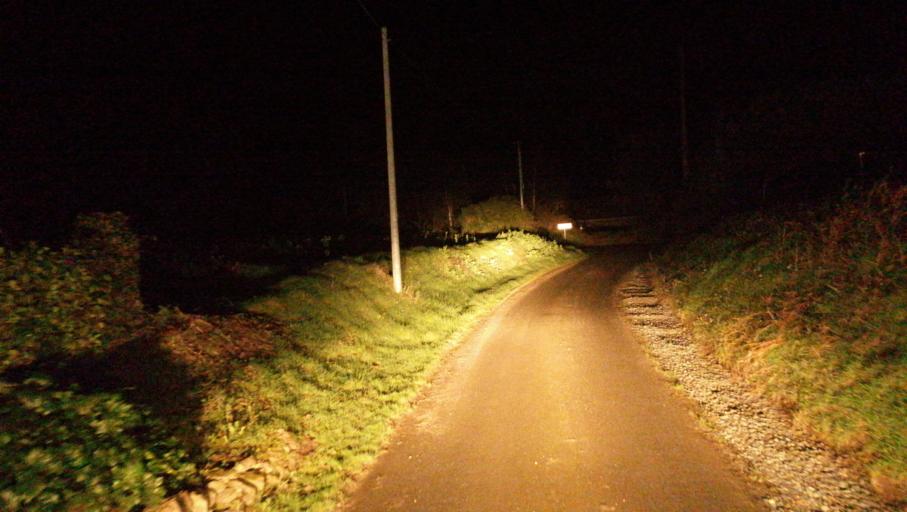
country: FR
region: Brittany
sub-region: Departement des Cotes-d'Armor
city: Lanvollon
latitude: 48.6373
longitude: -3.0064
